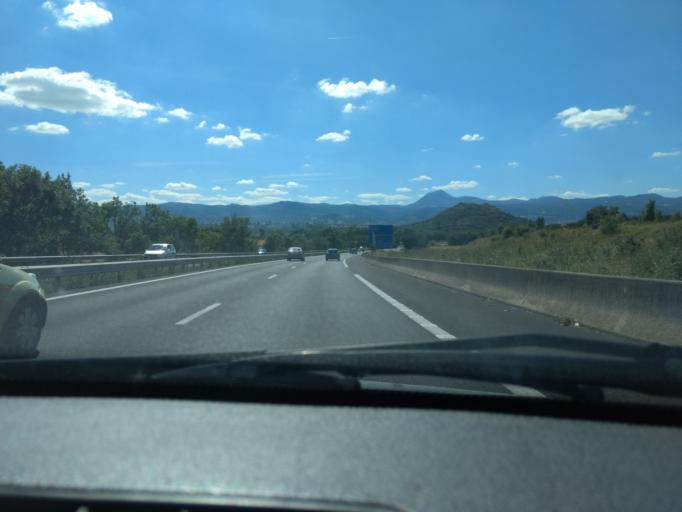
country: FR
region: Auvergne
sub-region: Departement du Puy-de-Dome
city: Aulnat
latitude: 45.7718
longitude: 3.1557
